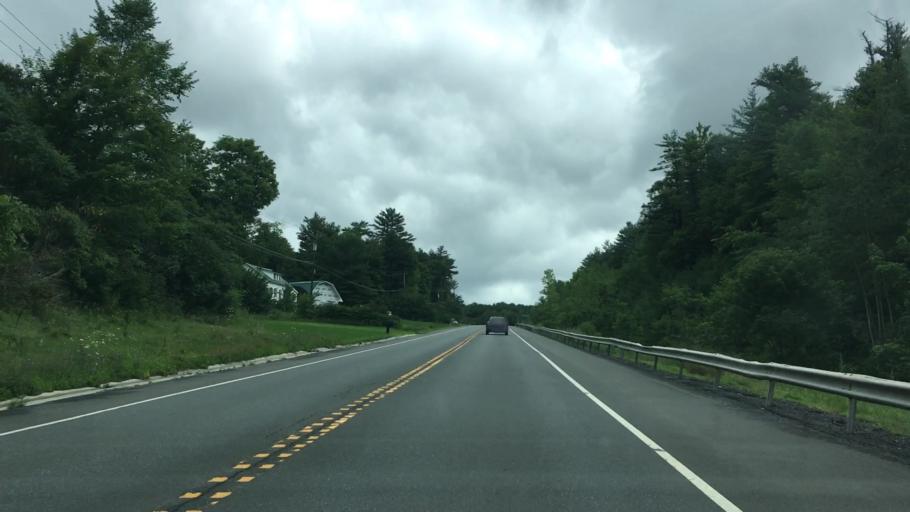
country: US
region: New York
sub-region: Rensselaer County
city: Hoosick Falls
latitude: 42.8477
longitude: -73.3997
